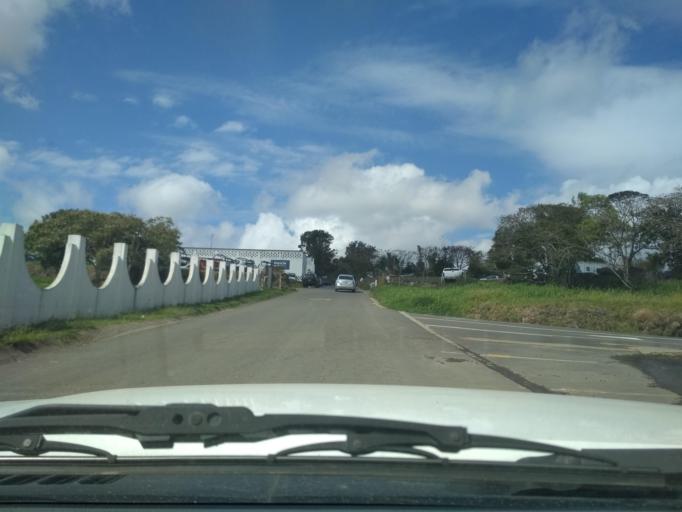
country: MX
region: Veracruz
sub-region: Emiliano Zapata
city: Dos Rios
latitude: 19.4850
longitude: -96.8116
